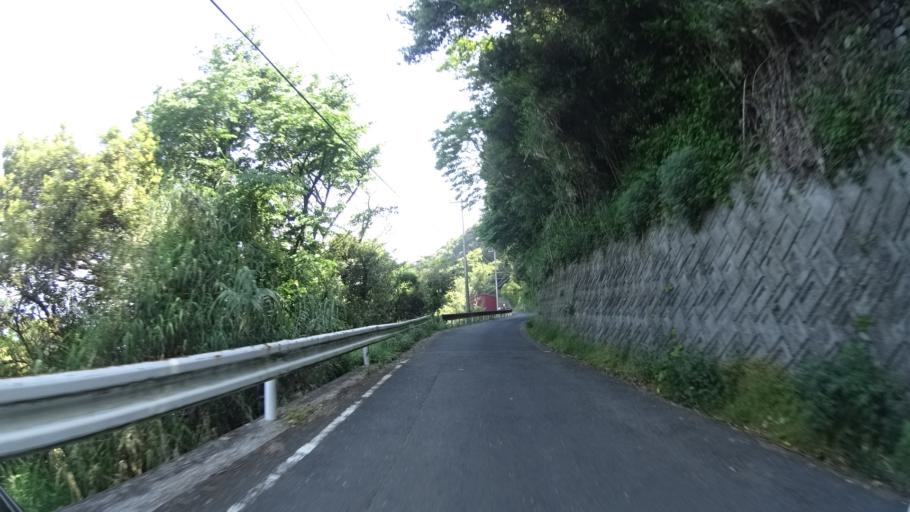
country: JP
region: Oita
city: Tsukumiura
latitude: 33.3506
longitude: 132.0290
